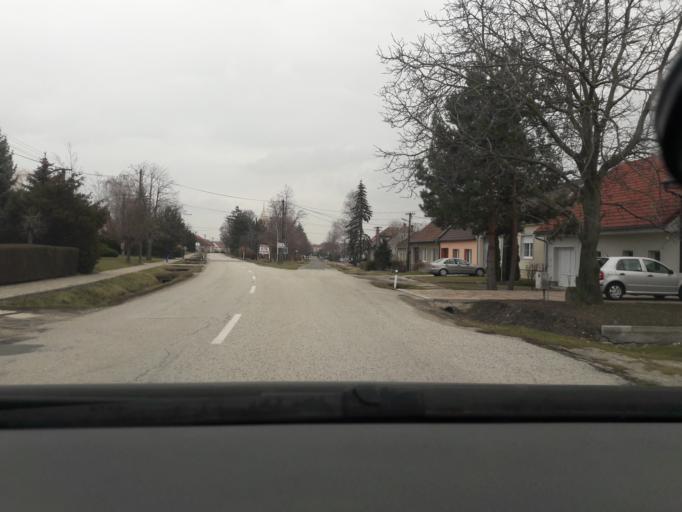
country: SK
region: Bratislavsky
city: Modra
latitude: 48.3862
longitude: 17.3951
